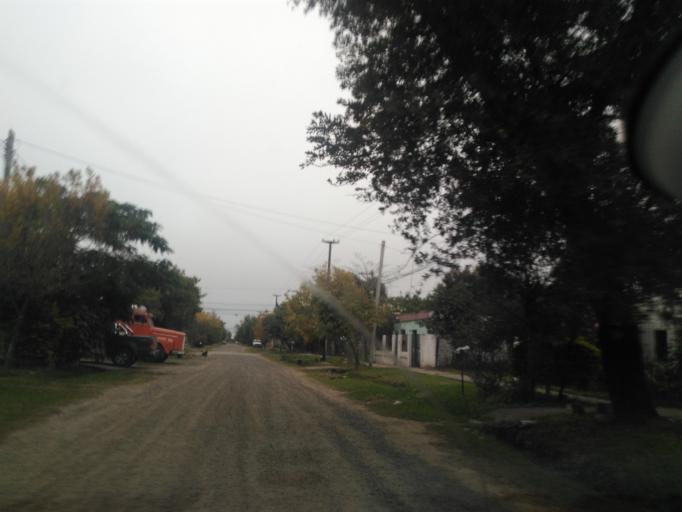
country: AR
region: Chaco
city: Resistencia
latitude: -27.4730
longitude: -59.0004
